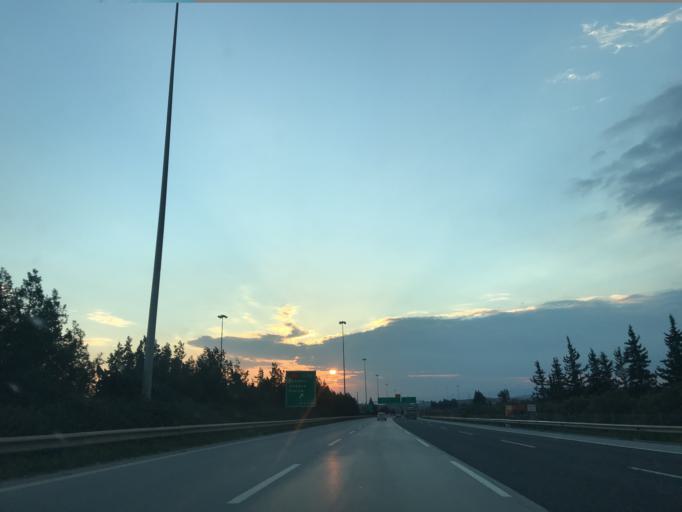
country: TR
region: Mersin
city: Yenice
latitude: 37.0092
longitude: 34.9781
